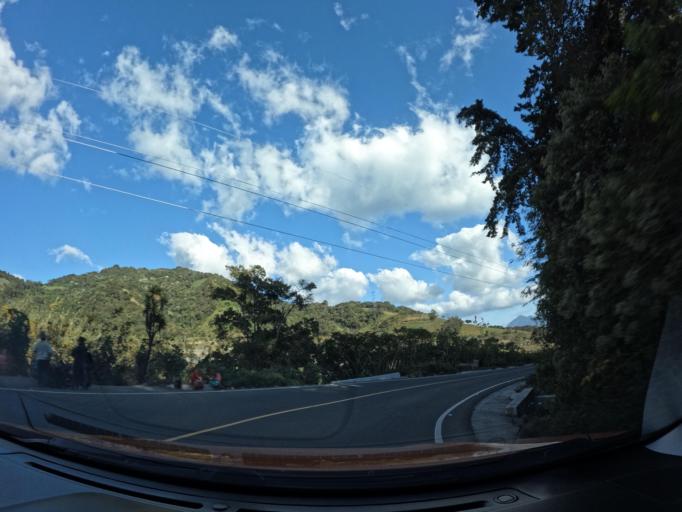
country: GT
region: Sacatepequez
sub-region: Municipio de Santa Maria de Jesus
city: Santa Maria de Jesus
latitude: 14.4774
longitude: -90.6954
